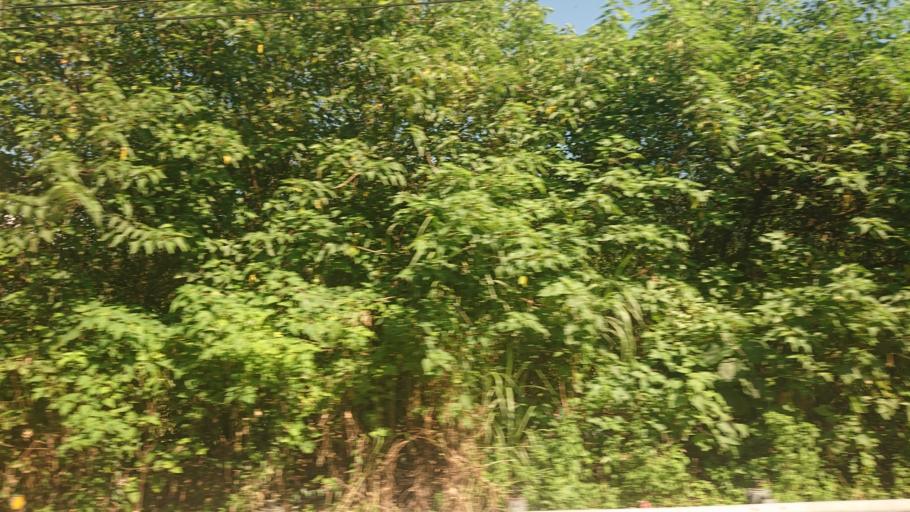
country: TW
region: Taiwan
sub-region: Nantou
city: Puli
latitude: 24.0598
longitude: 120.9386
